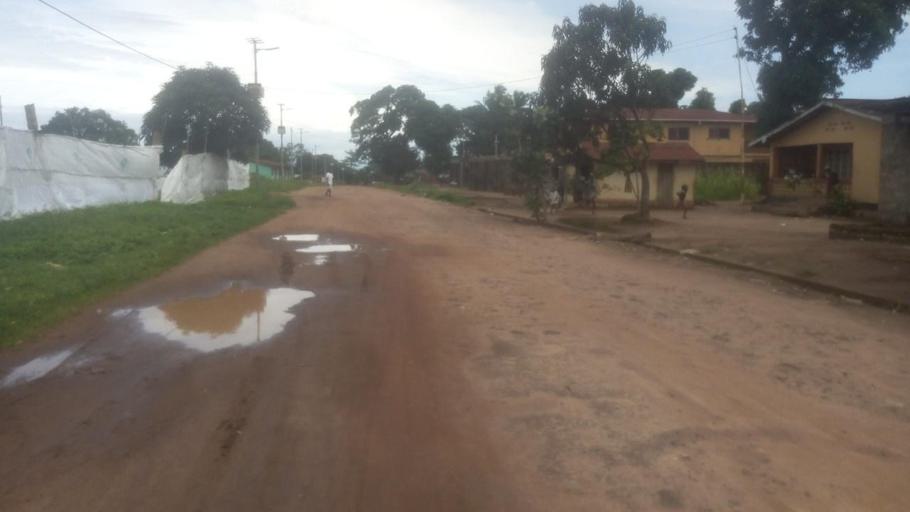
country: SL
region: Northern Province
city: Masoyila
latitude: 8.6018
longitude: -13.1980
